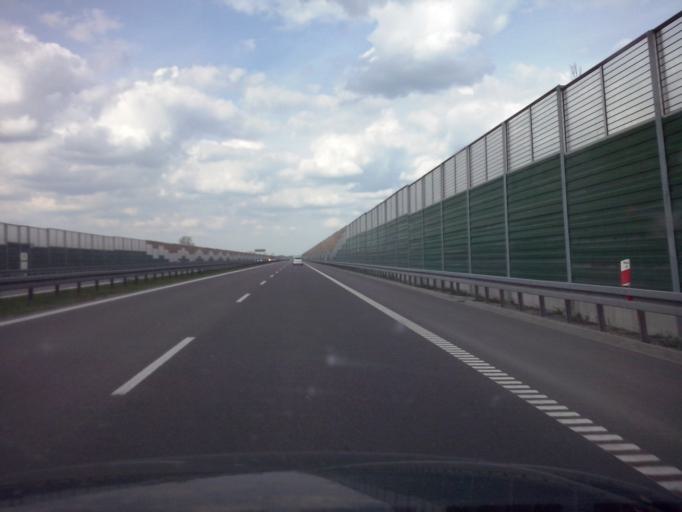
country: PL
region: Subcarpathian Voivodeship
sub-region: Powiat rzeszowski
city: Trzebownisko
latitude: 50.1022
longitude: 22.0660
